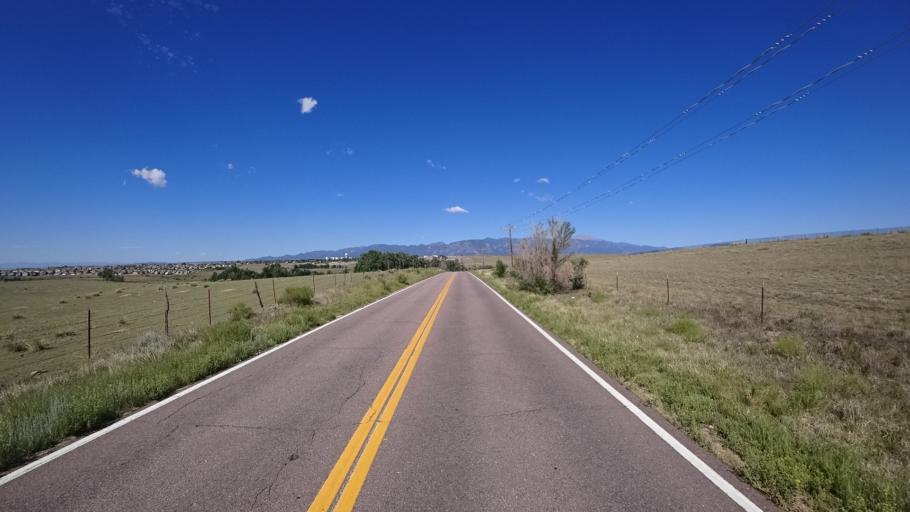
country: US
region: Colorado
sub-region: El Paso County
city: Security-Widefield
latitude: 38.7374
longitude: -104.6594
